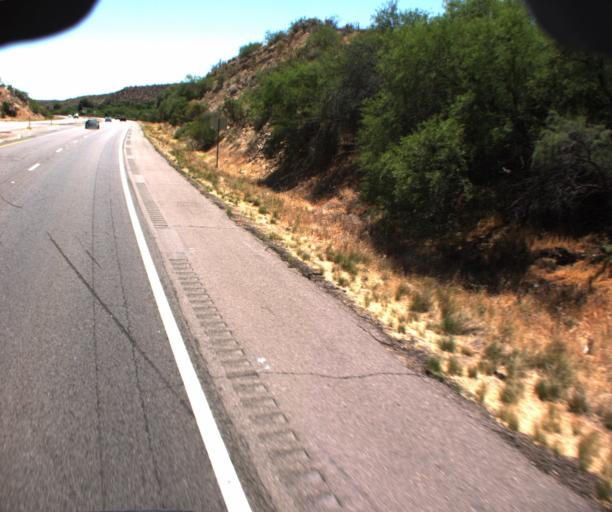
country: US
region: Arizona
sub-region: Maricopa County
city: Wickenburg
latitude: 33.9165
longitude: -112.6767
